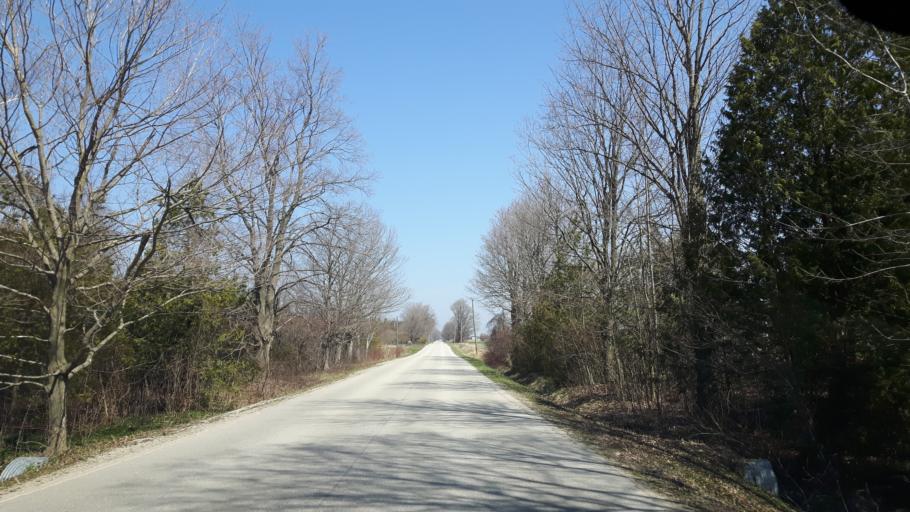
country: CA
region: Ontario
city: Goderich
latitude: 43.6257
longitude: -81.6846
